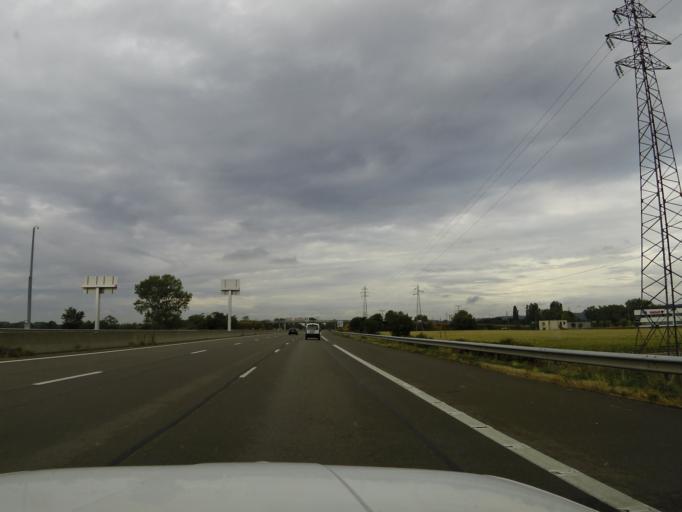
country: FR
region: Rhone-Alpes
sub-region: Departement de l'Ain
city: Thil
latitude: 45.8279
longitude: 5.0174
